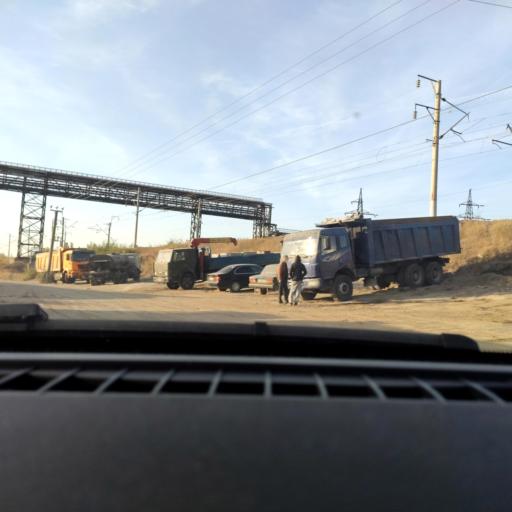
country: RU
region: Voronezj
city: Maslovka
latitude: 51.6256
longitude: 39.2575
